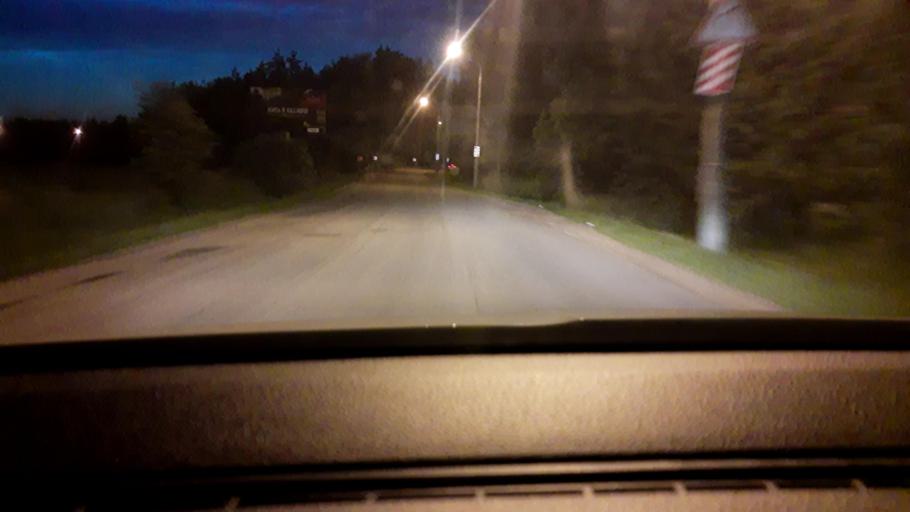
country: RU
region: Moskovskaya
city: Pavlovskaya Sloboda
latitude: 55.7821
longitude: 37.0761
